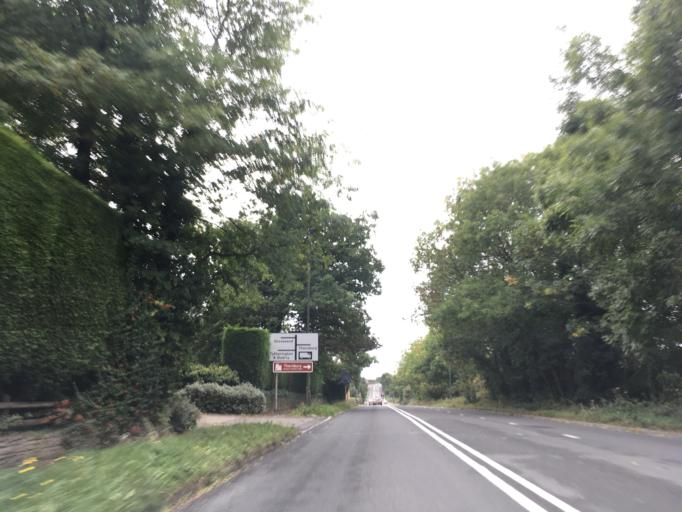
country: GB
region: England
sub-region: South Gloucestershire
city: Tytherington
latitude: 51.6016
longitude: -2.4980
